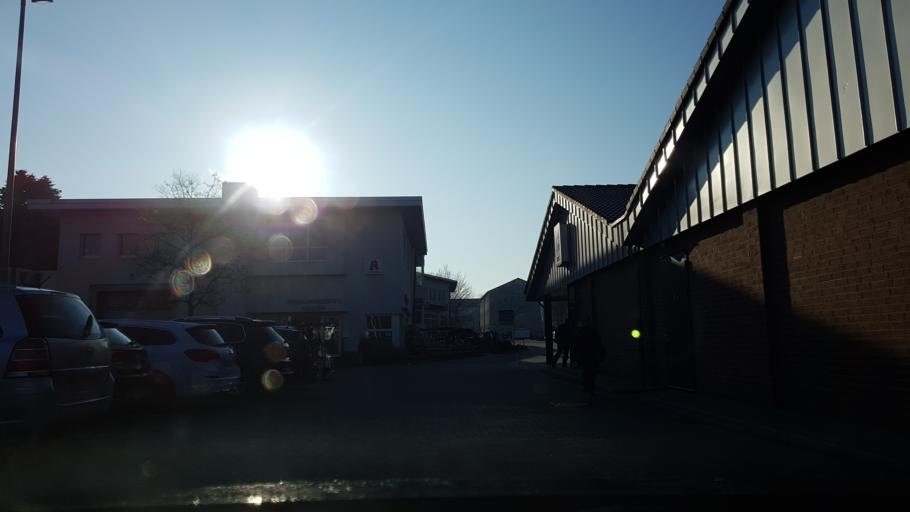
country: DE
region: North Rhine-Westphalia
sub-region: Regierungsbezirk Dusseldorf
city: Muelheim (Ruhr)
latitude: 51.4350
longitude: 6.9178
